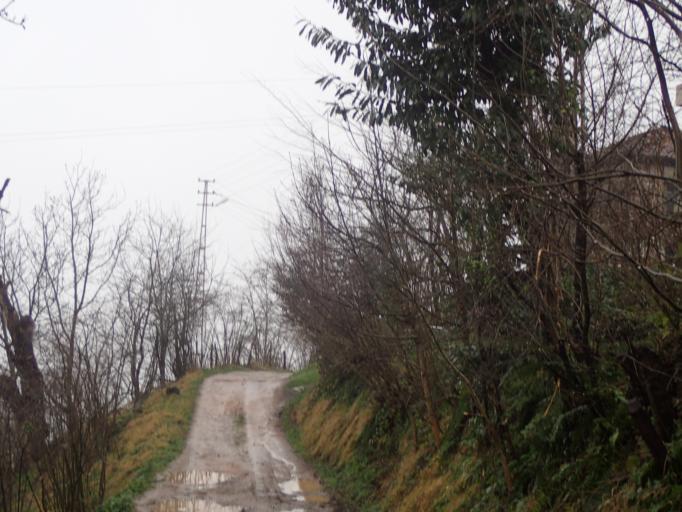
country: TR
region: Ordu
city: Camas
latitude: 40.9121
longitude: 37.5673
